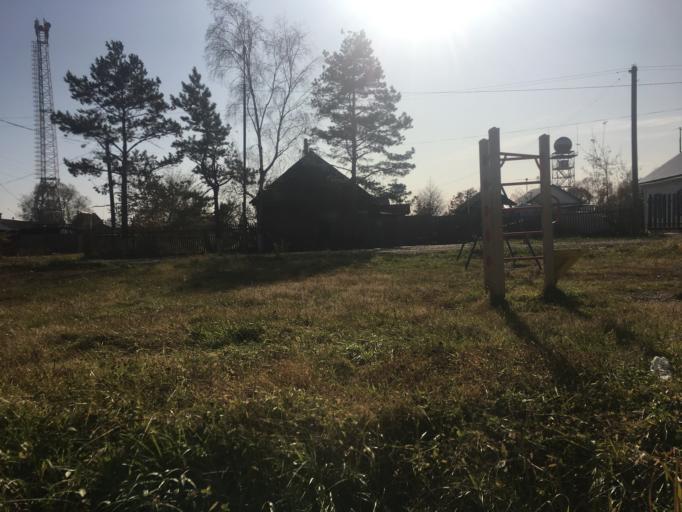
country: RU
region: Primorskiy
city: Dal'nerechensk
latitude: 45.8810
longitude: 133.7276
